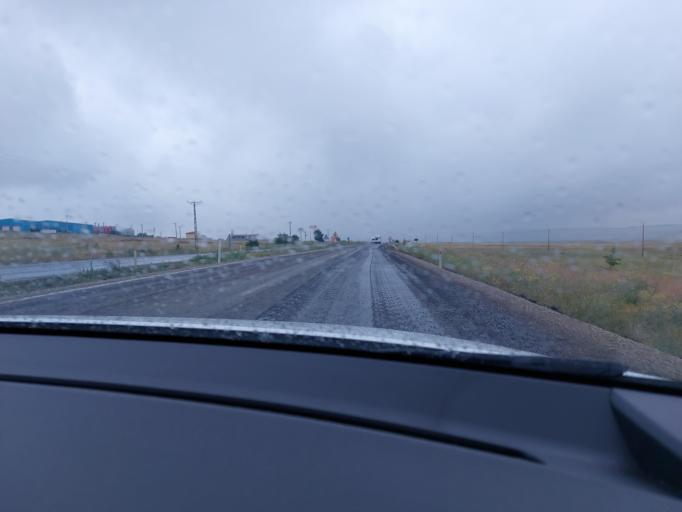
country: TR
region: Nevsehir
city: Dobada
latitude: 38.5364
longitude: 34.4494
